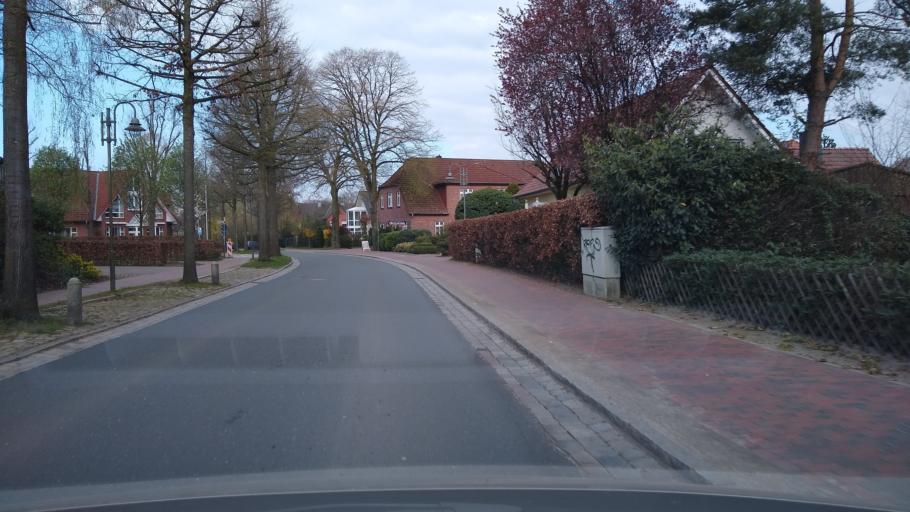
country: DE
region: Lower Saxony
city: Emstek
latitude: 52.8339
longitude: 8.1476
